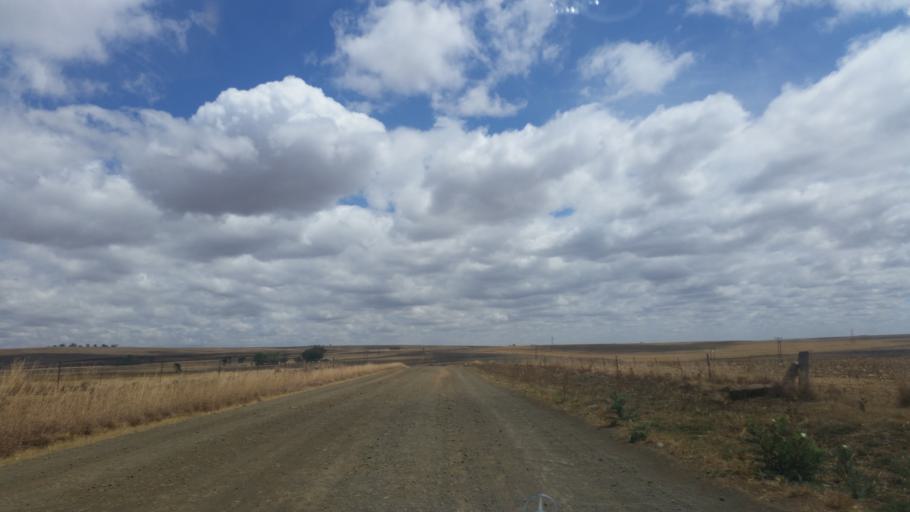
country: ZA
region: Orange Free State
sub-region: Thabo Mofutsanyana District Municipality
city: Harrismith
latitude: -28.2521
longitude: 28.9348
